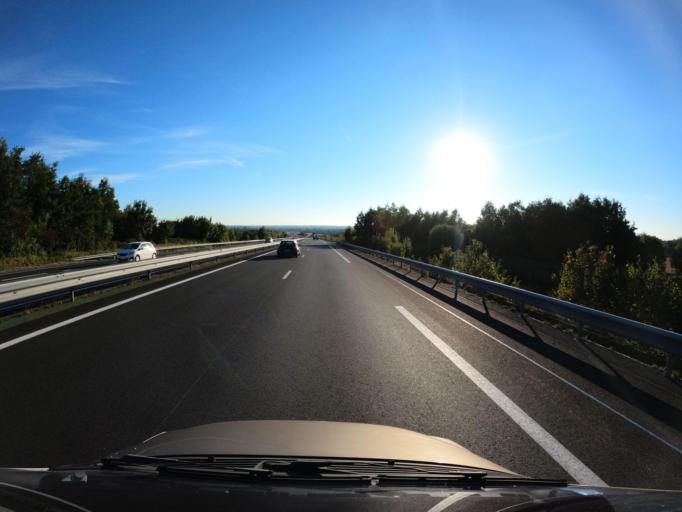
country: FR
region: Pays de la Loire
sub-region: Departement de la Vendee
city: La Gaubretiere
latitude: 46.9173
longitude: -1.0396
